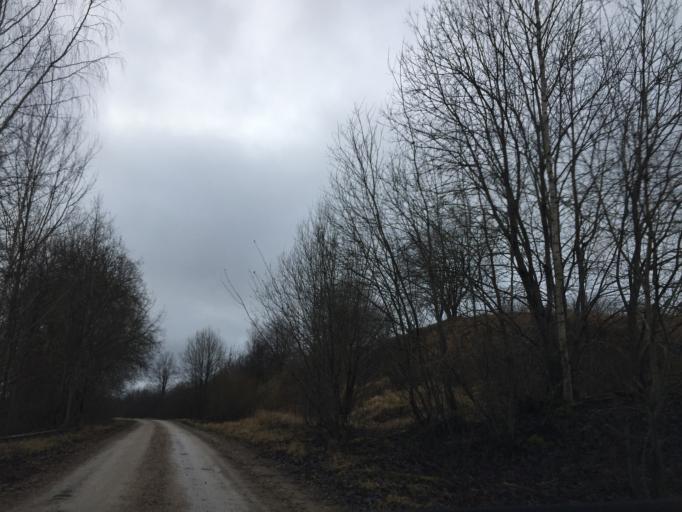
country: LV
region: Broceni
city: Broceni
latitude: 56.6711
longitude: 22.5566
